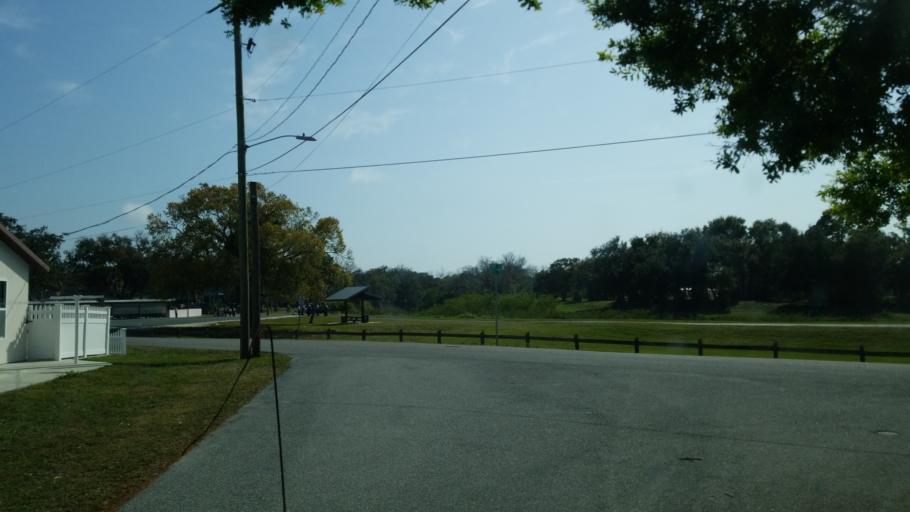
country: US
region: Florida
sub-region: Sarasota County
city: Southgate
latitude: 27.3222
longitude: -82.5039
